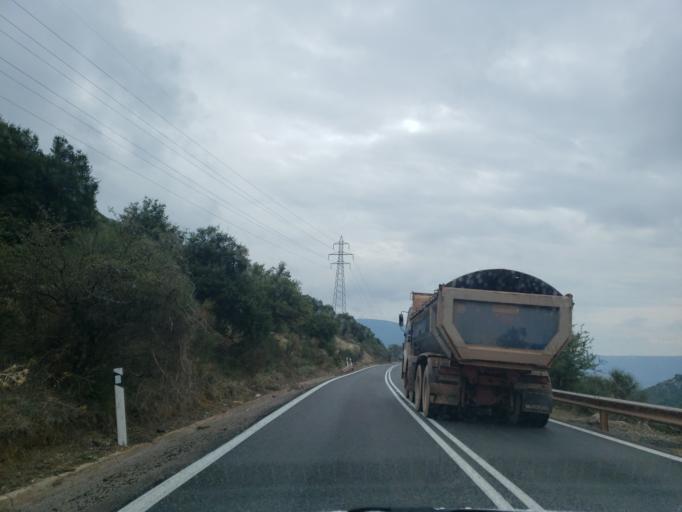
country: GR
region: Central Greece
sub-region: Nomos Fokidos
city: Amfissa
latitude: 38.5681
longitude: 22.3985
